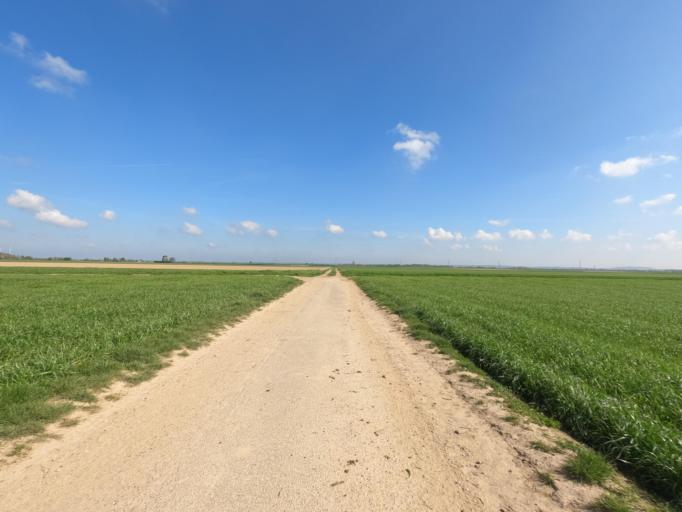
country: DE
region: North Rhine-Westphalia
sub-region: Regierungsbezirk Koln
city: Heinsberg
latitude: 51.0356
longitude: 6.0798
